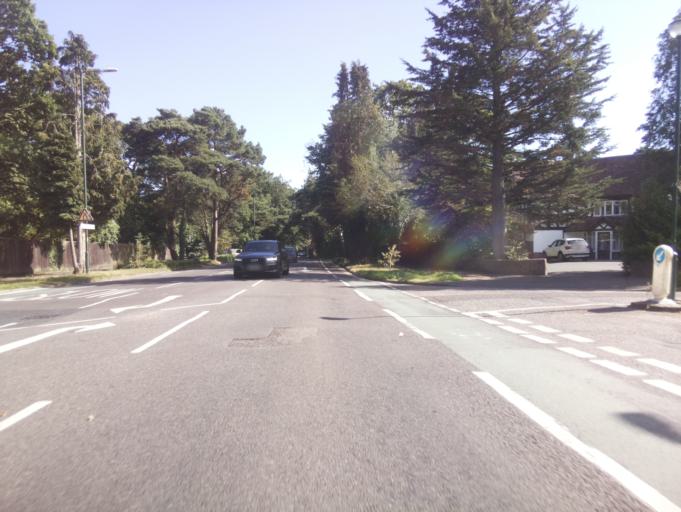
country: GB
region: England
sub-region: Bournemouth
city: Bournemouth
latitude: 50.7334
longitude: -1.8939
